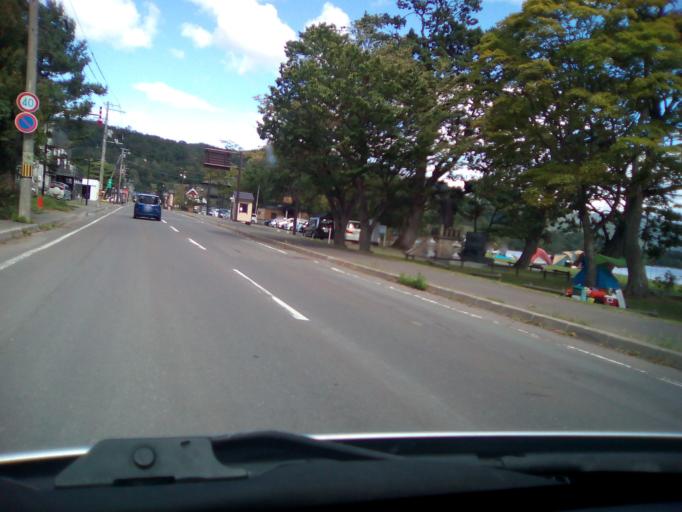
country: JP
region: Hokkaido
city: Date
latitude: 42.6447
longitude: 140.8295
